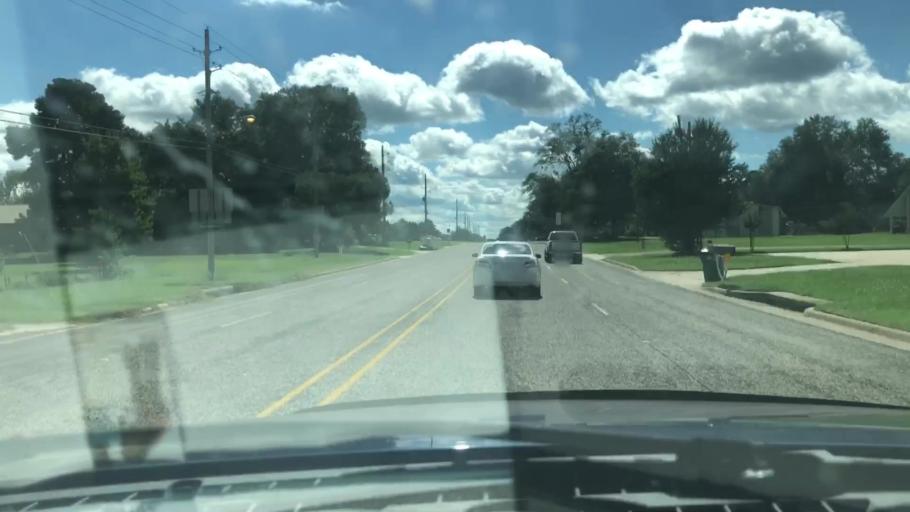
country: US
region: Texas
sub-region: Bowie County
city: Wake Village
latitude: 33.3945
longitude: -94.0922
